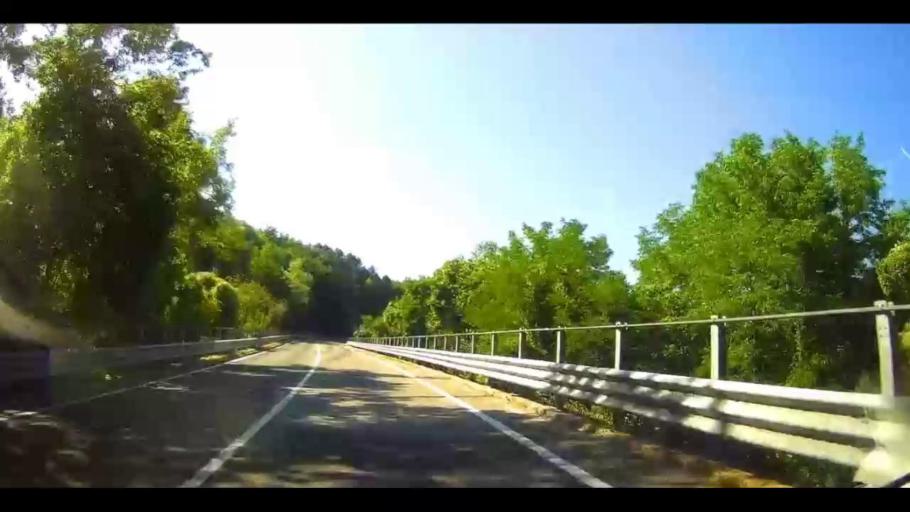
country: IT
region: Calabria
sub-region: Provincia di Cosenza
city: Spezzano Piccolo
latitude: 39.2983
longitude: 16.3555
